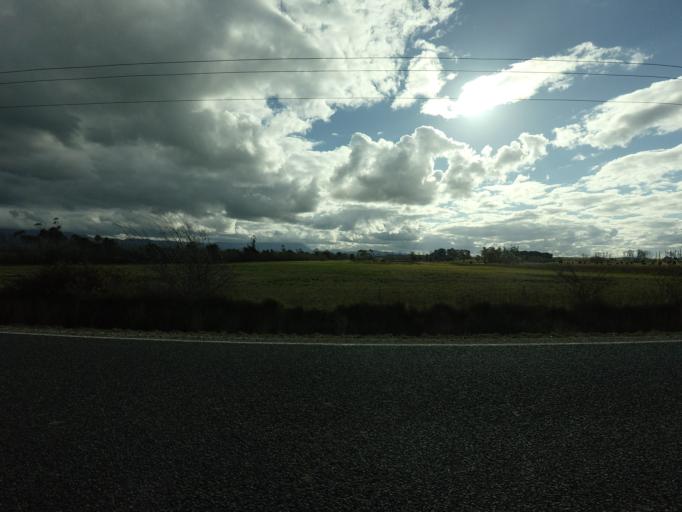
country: AU
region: Tasmania
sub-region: Northern Midlands
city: Longford
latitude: -41.7233
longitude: 147.0895
